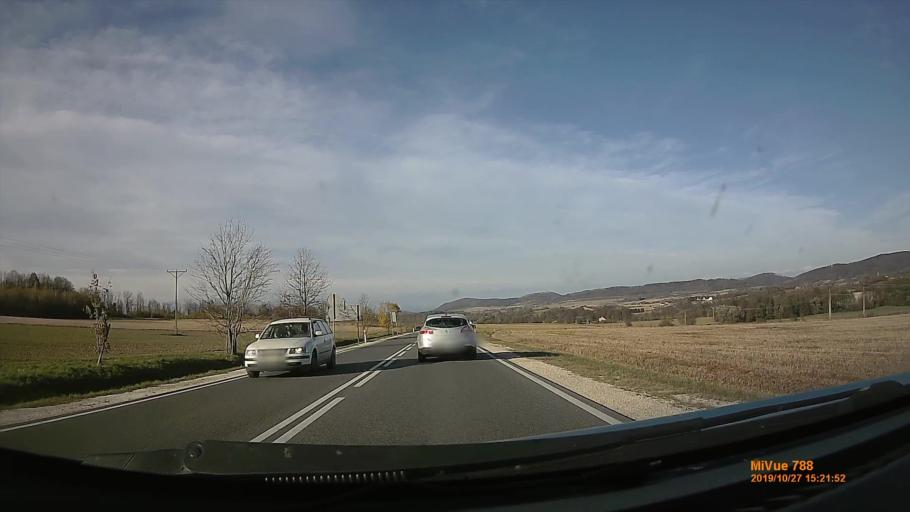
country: PL
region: Lower Silesian Voivodeship
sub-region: Powiat klodzki
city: Bystrzyca Klodzka
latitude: 50.2939
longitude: 16.6630
